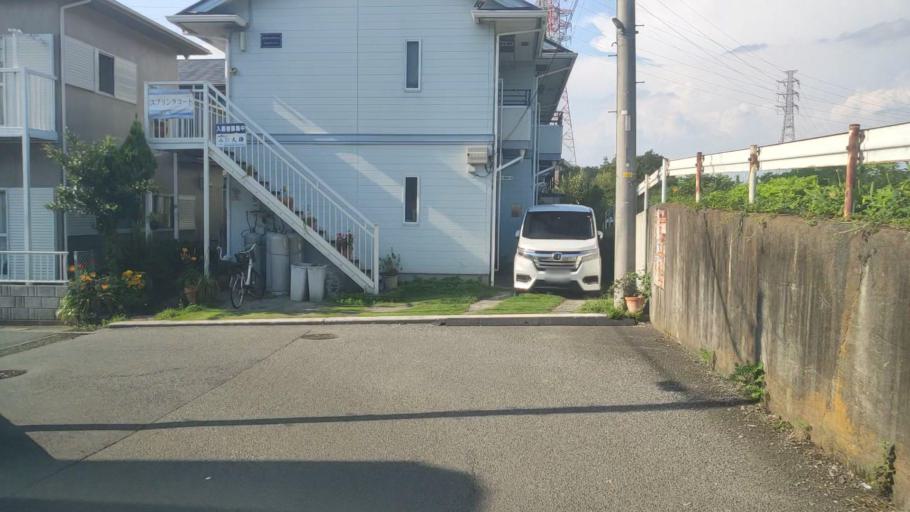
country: JP
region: Kanagawa
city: Hiratsuka
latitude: 35.3464
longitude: 139.3231
